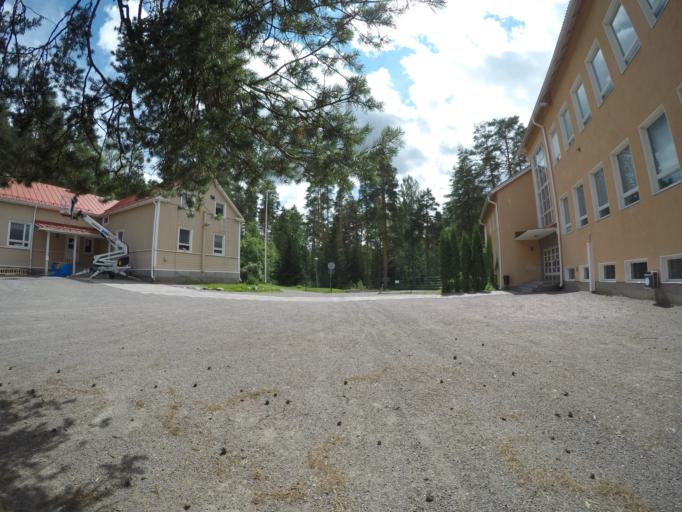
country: FI
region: Haeme
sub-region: Haemeenlinna
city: Haemeenlinna
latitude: 60.9729
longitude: 24.4253
